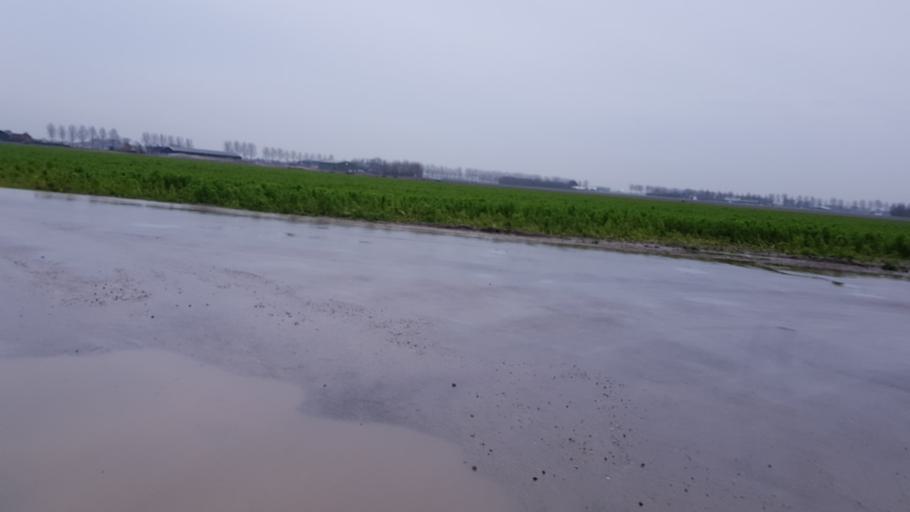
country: NL
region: North Holland
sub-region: Gemeente Haarlemmermeer
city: Hoofddorp
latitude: 52.2853
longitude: 4.6893
